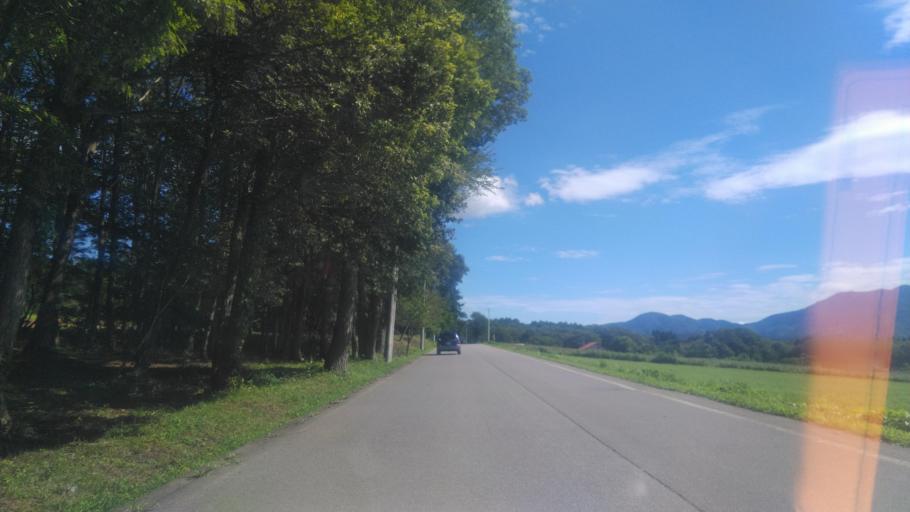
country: JP
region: Nagano
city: Nagano-shi
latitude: 36.7831
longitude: 138.1774
